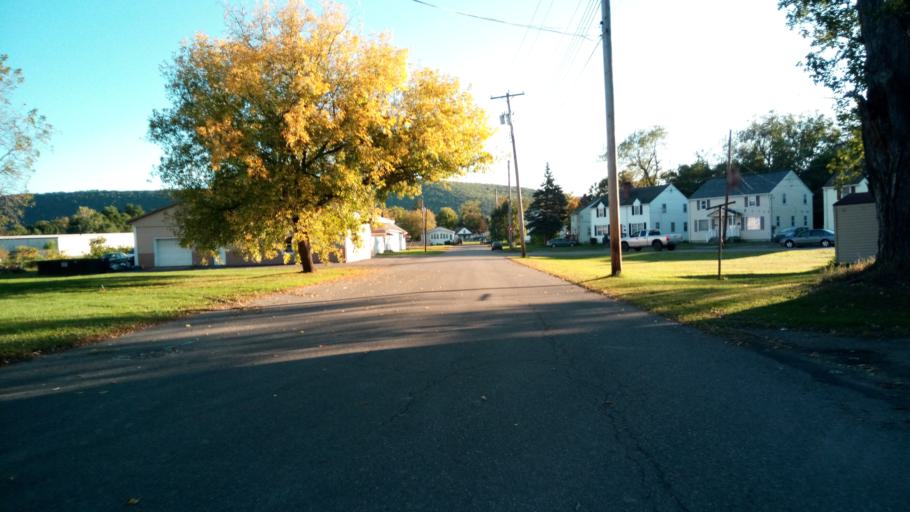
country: US
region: New York
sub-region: Chemung County
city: Southport
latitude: 42.0655
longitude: -76.8055
